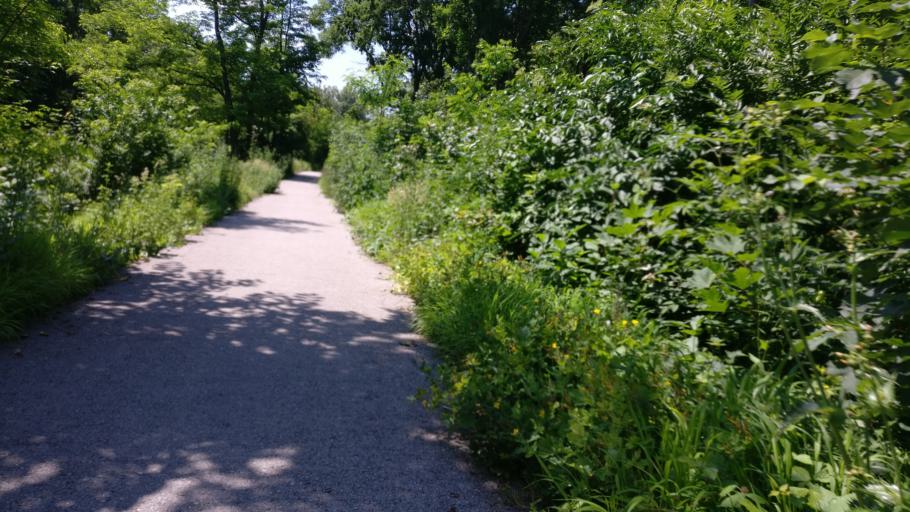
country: AT
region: Lower Austria
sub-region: Politischer Bezirk Baden
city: Oberwaltersdorf
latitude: 47.9690
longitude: 16.3139
